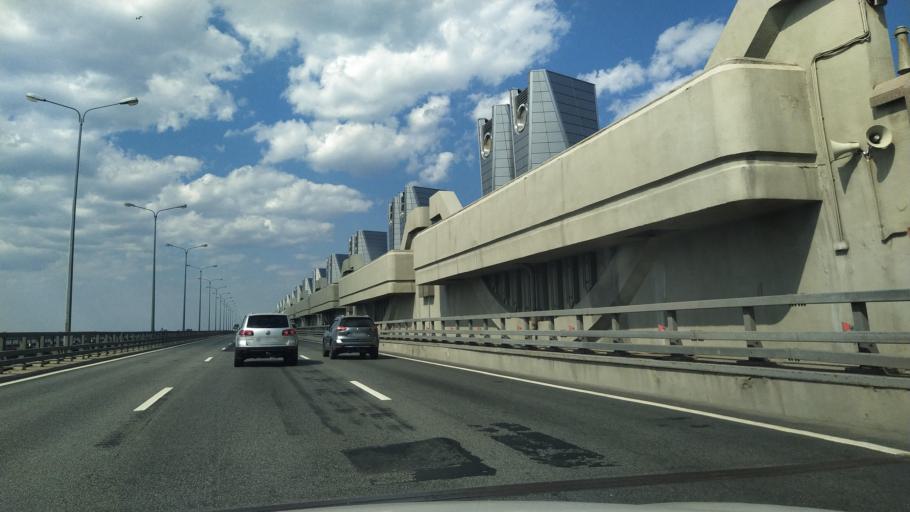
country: RU
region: Leningrad
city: Gorskaya
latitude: 60.0366
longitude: 29.9555
